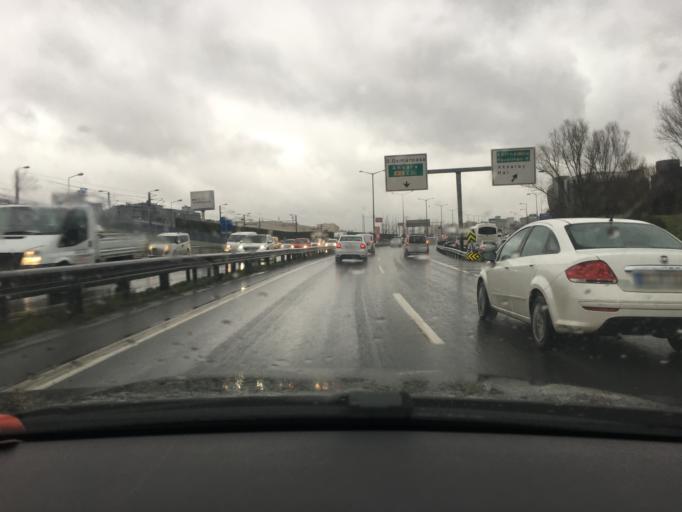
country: TR
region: Istanbul
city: Esenler
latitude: 41.0380
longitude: 28.8886
